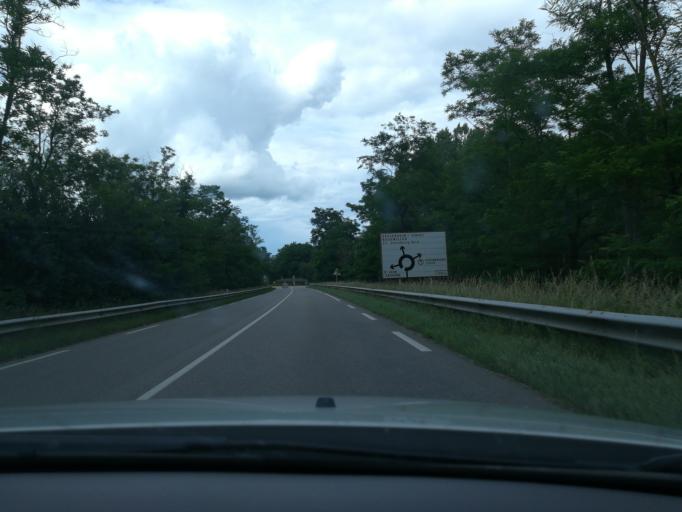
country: FR
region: Alsace
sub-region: Departement du Bas-Rhin
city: Steinbourg
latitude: 48.7665
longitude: 7.4013
